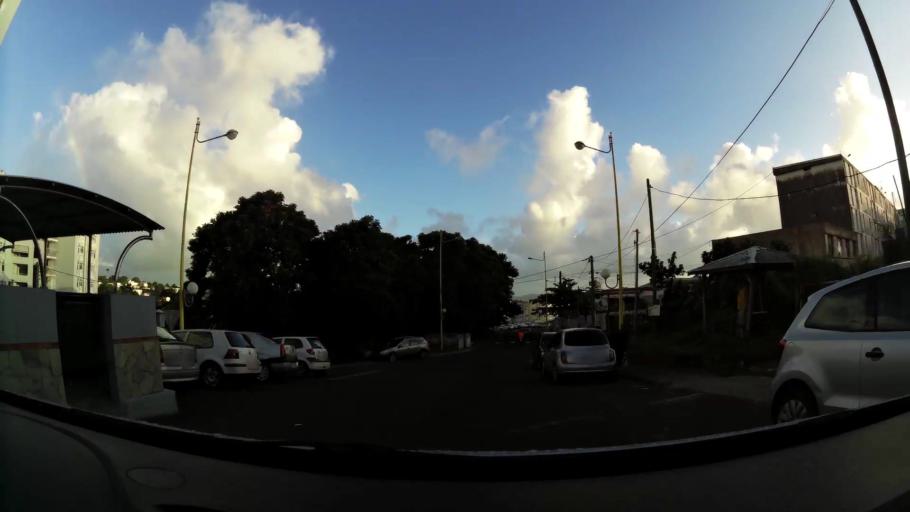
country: MQ
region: Martinique
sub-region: Martinique
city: Fort-de-France
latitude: 14.6333
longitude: -61.0681
